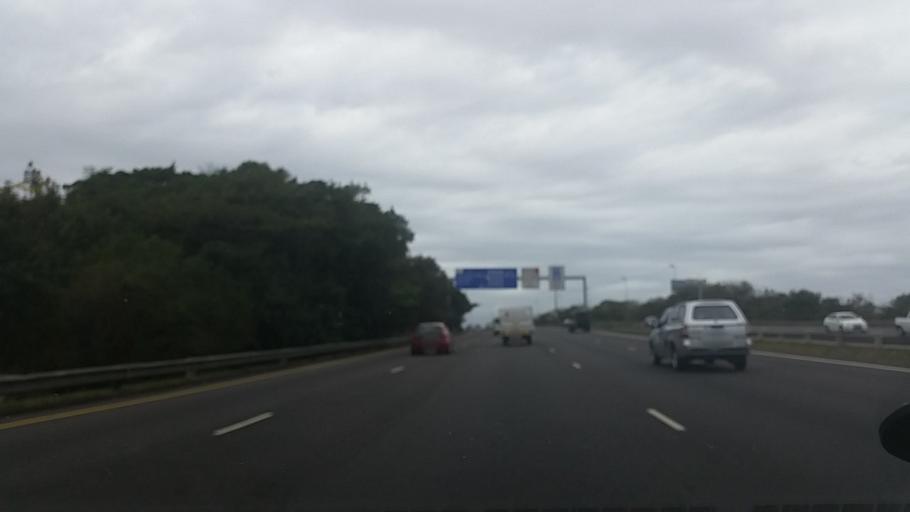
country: ZA
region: KwaZulu-Natal
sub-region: eThekwini Metropolitan Municipality
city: Berea
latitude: -29.8394
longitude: 30.9678
